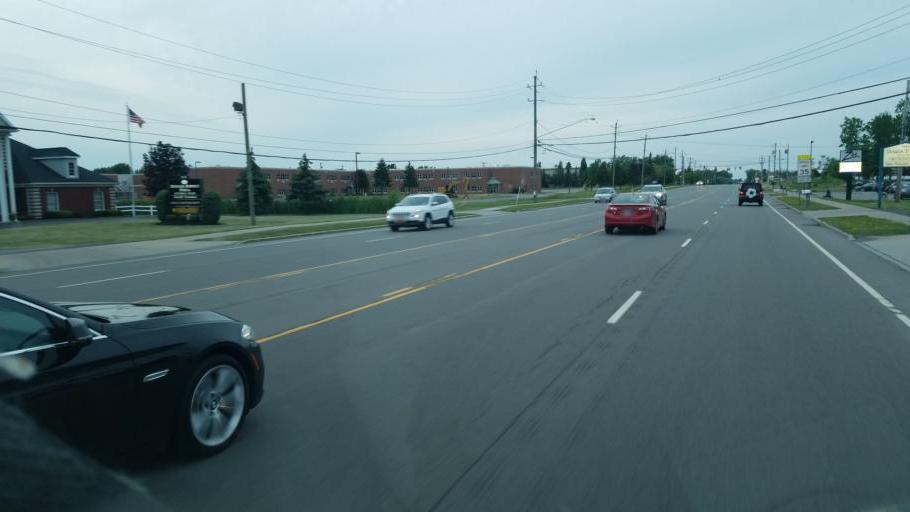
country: US
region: New York
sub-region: Erie County
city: Harris Hill
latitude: 43.0024
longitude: -78.6968
